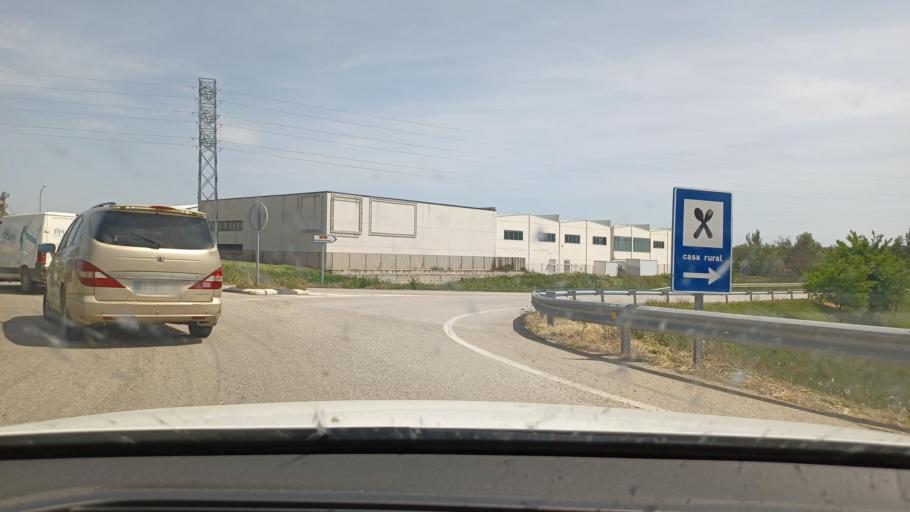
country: ES
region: Castille and Leon
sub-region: Provincia de Soria
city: Almazan
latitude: 41.4707
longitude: -2.5399
